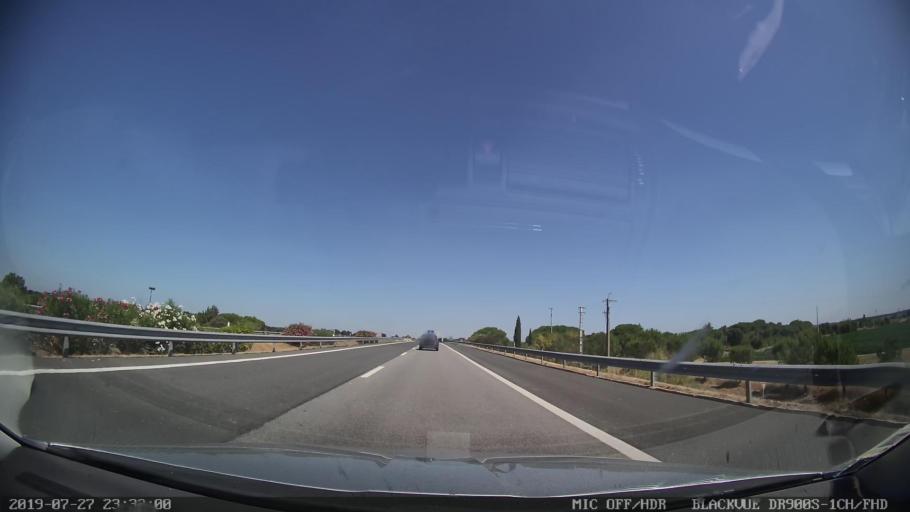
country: PT
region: Evora
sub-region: Montemor-O-Novo
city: Montemor-o-Novo
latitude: 38.6586
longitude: -8.1688
